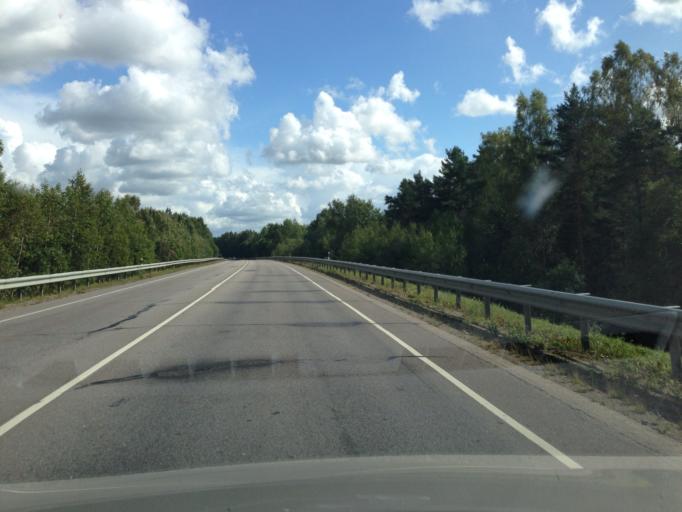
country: EE
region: Harju
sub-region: Saku vald
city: Saku
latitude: 59.3133
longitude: 24.6873
